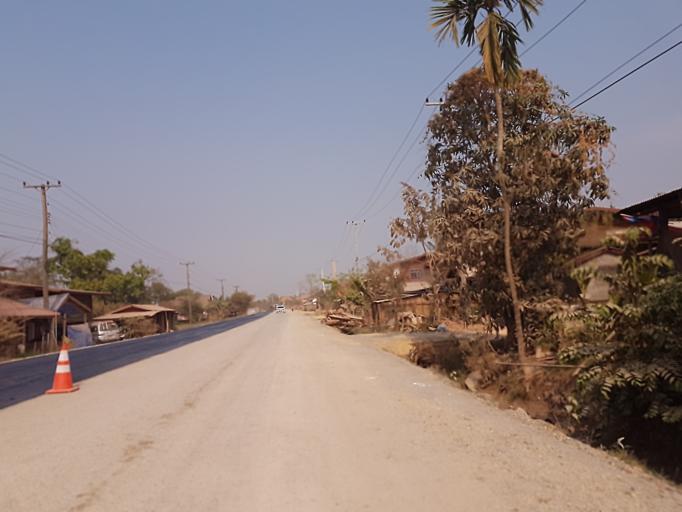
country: TH
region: Nong Khai
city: Nong Khai
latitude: 17.9354
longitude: 102.7827
